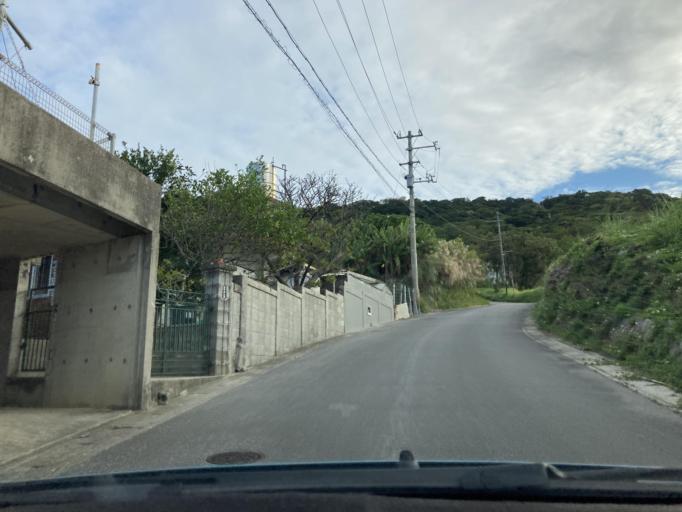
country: JP
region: Okinawa
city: Ginowan
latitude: 26.1668
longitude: 127.7865
